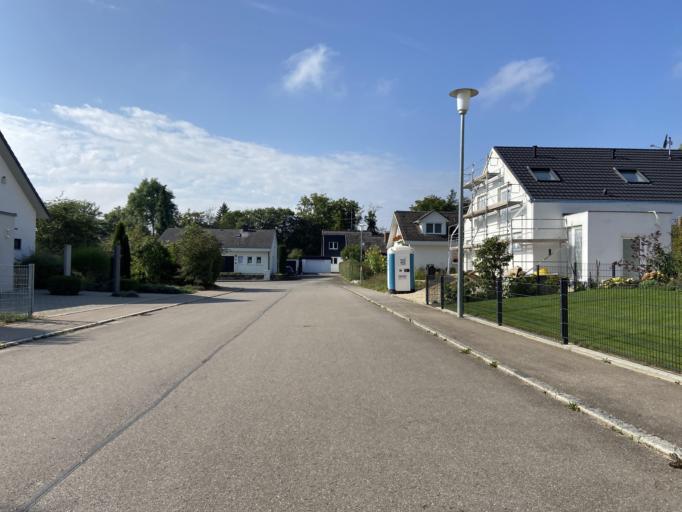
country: DE
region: Baden-Wuerttemberg
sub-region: Tuebingen Region
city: Inzigkofen
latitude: 48.0934
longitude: 9.1924
